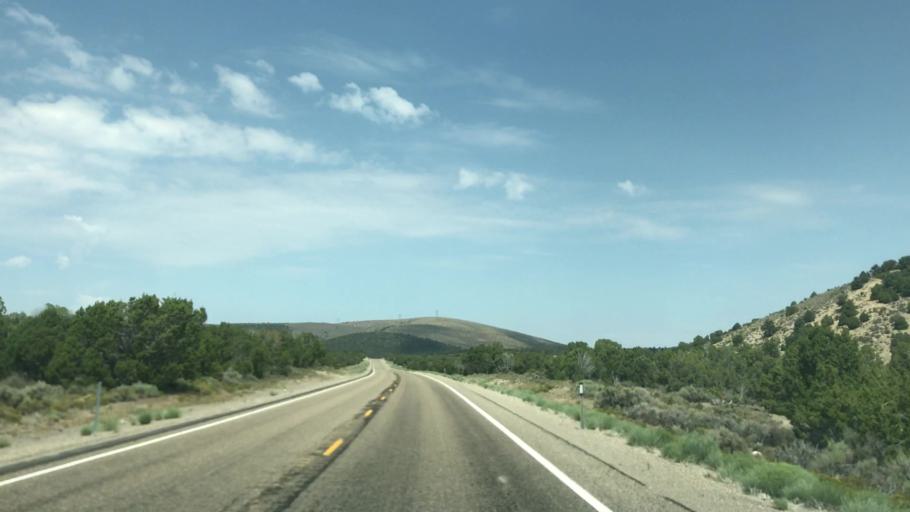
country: US
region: Nevada
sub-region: White Pine County
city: Ely
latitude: 39.3828
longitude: -115.0686
